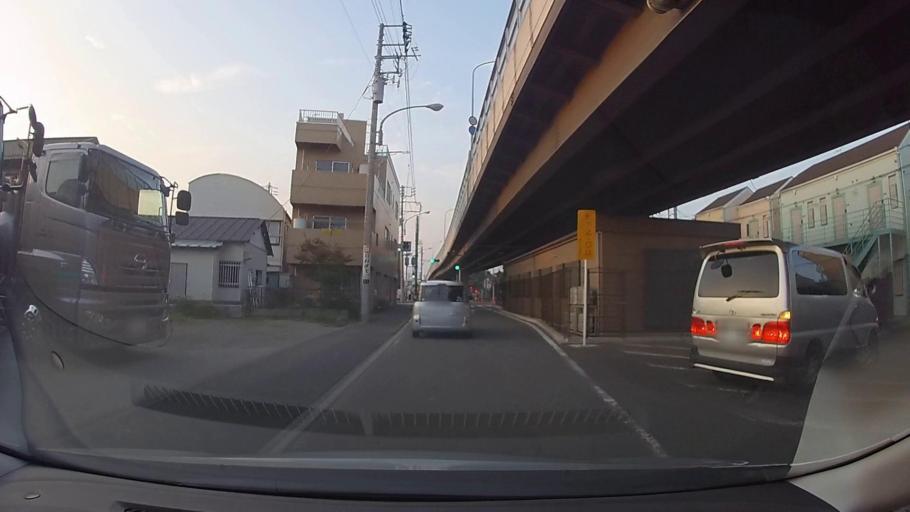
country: JP
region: Kanagawa
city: Minami-rinkan
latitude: 35.4690
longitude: 139.4804
